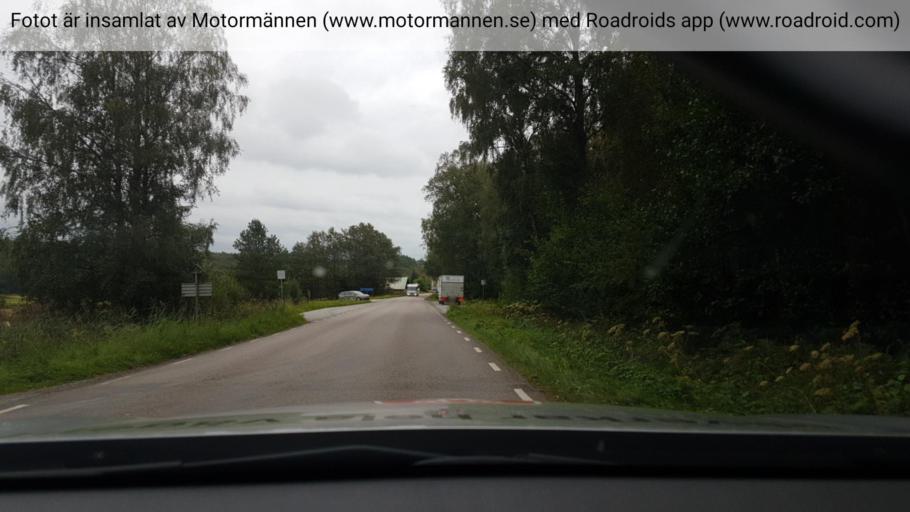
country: SE
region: Vaestra Goetaland
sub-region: Tanums Kommun
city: Grebbestad
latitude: 58.6721
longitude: 11.2927
